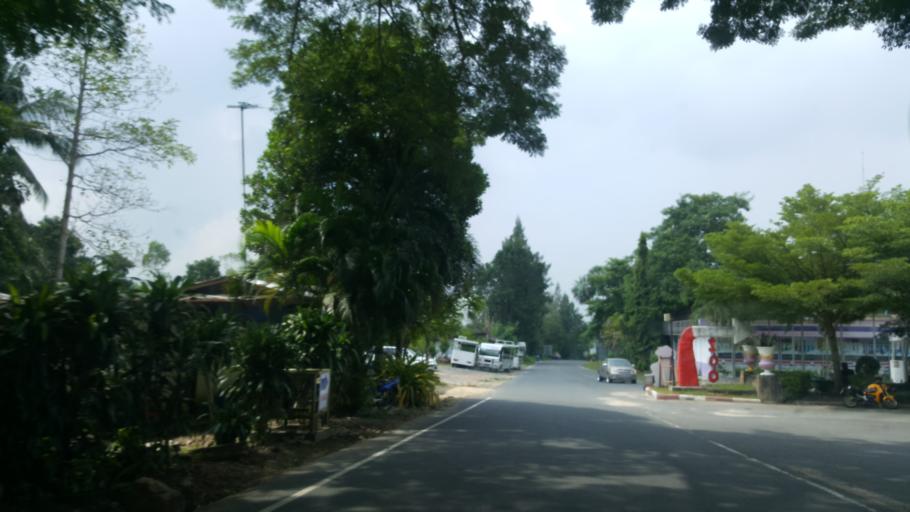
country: TH
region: Chon Buri
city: Ban Bueng
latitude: 13.2149
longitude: 101.0576
